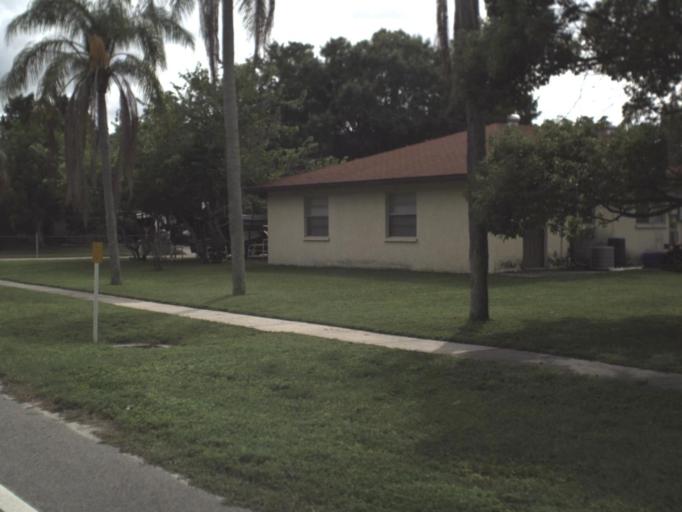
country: US
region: Florida
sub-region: Manatee County
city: Samoset
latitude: 27.4804
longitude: -82.5467
